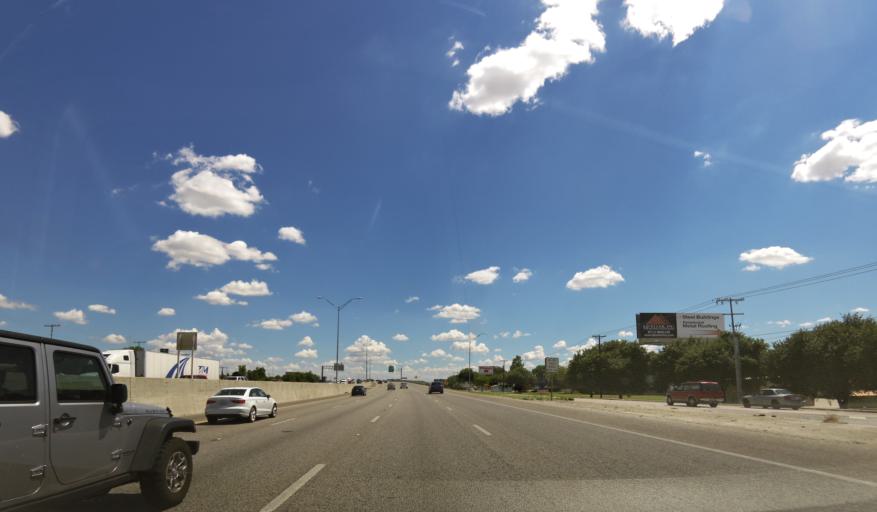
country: US
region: Texas
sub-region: Comal County
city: New Braunfels
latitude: 29.7179
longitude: -98.0881
